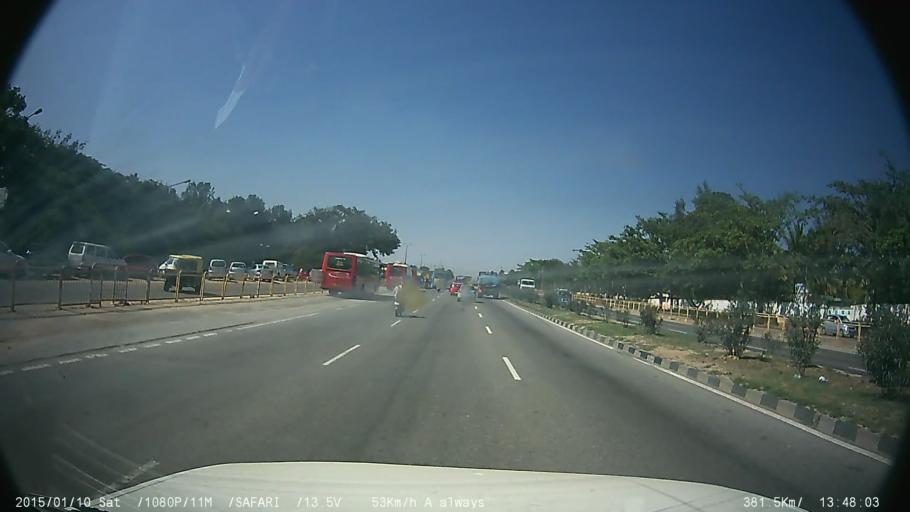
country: IN
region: Karnataka
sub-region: Bangalore Urban
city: Anekal
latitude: 12.8093
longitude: 77.6966
